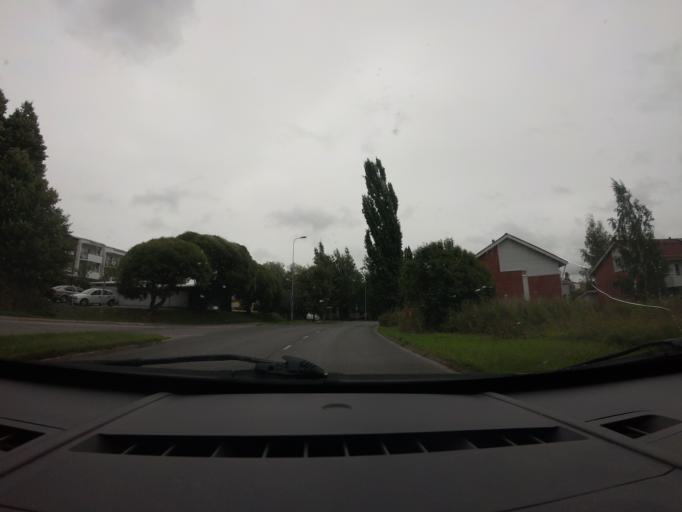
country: FI
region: Varsinais-Suomi
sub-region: Turku
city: Turku
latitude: 60.4134
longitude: 22.2983
